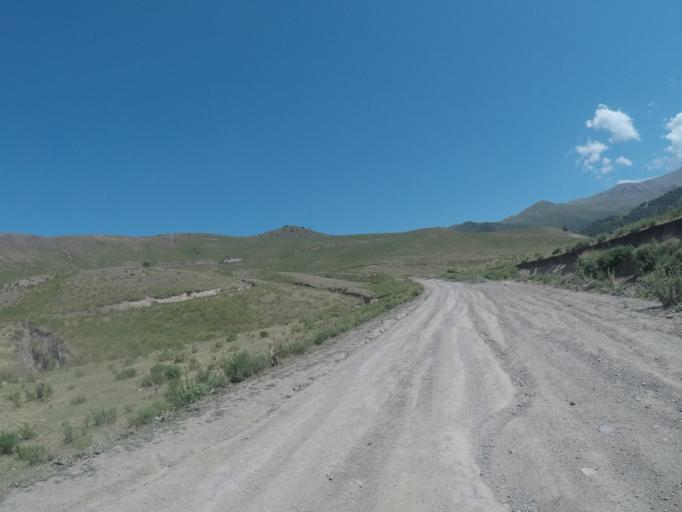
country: KG
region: Chuy
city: Bishkek
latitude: 42.6487
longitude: 74.5146
